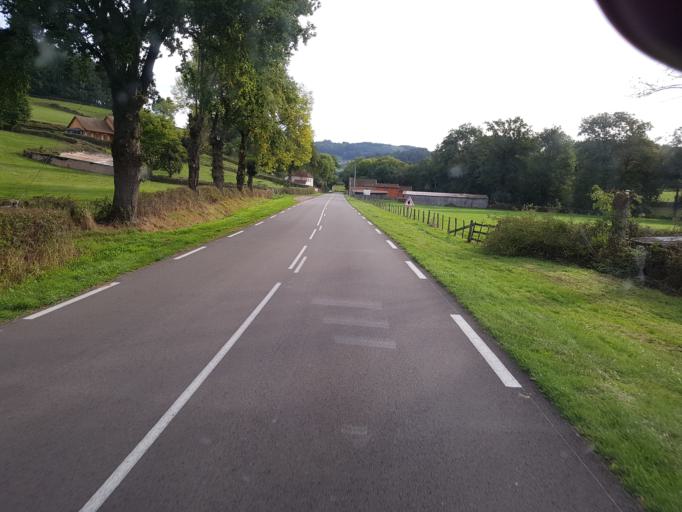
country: FR
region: Bourgogne
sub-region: Departement de Saone-et-Loire
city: La Clayette
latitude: 46.2802
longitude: 4.3641
